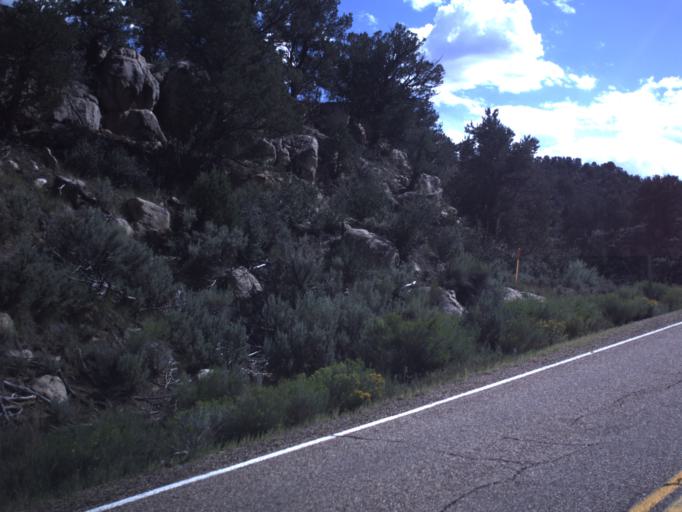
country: US
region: Utah
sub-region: Duchesne County
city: Duchesne
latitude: 40.3196
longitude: -110.6946
